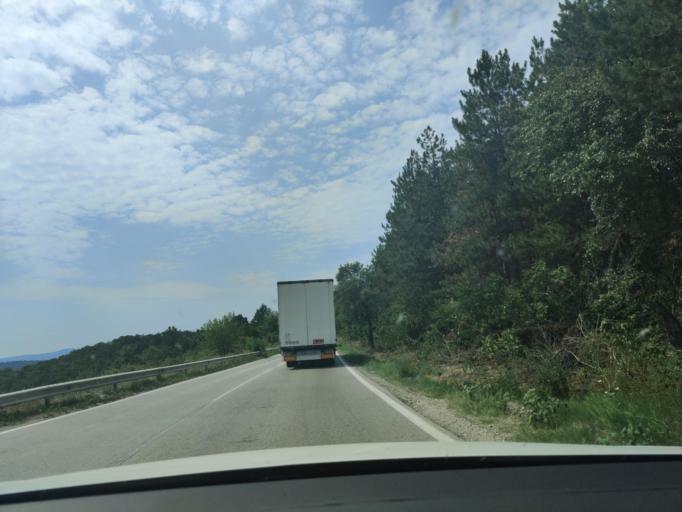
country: BG
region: Vidin
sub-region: Obshtina Dimovo
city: Dimovo
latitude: 43.7372
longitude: 22.7317
